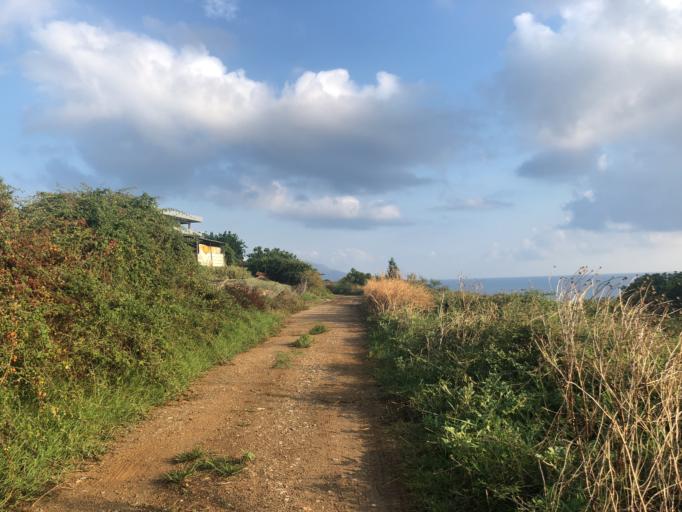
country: GR
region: Crete
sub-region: Nomos Chanias
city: Georgioupolis
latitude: 35.3460
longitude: 24.3122
